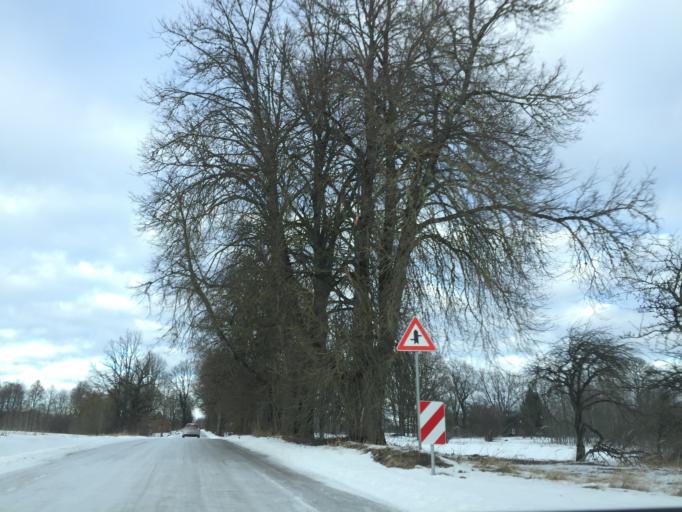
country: LV
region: Lielvarde
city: Lielvarde
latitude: 56.5631
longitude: 24.7346
